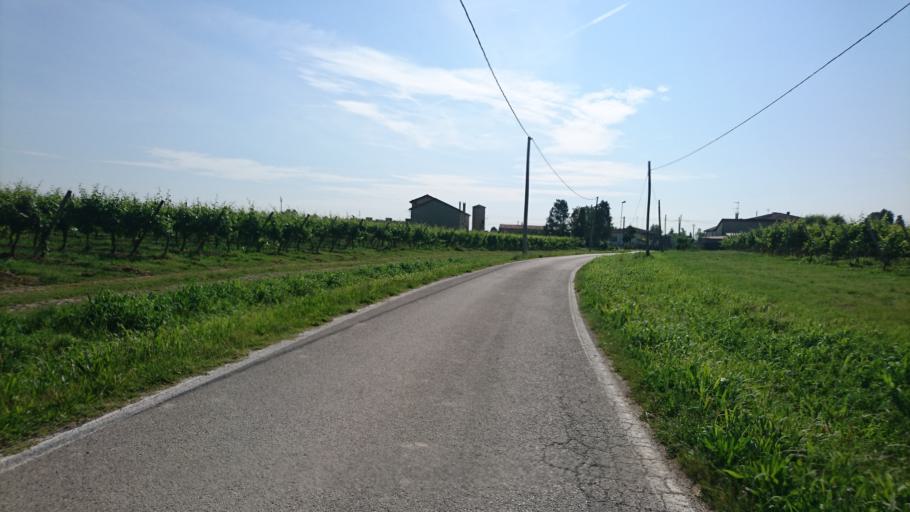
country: IT
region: Veneto
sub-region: Provincia di Padova
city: Merlara
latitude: 45.1744
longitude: 11.4380
